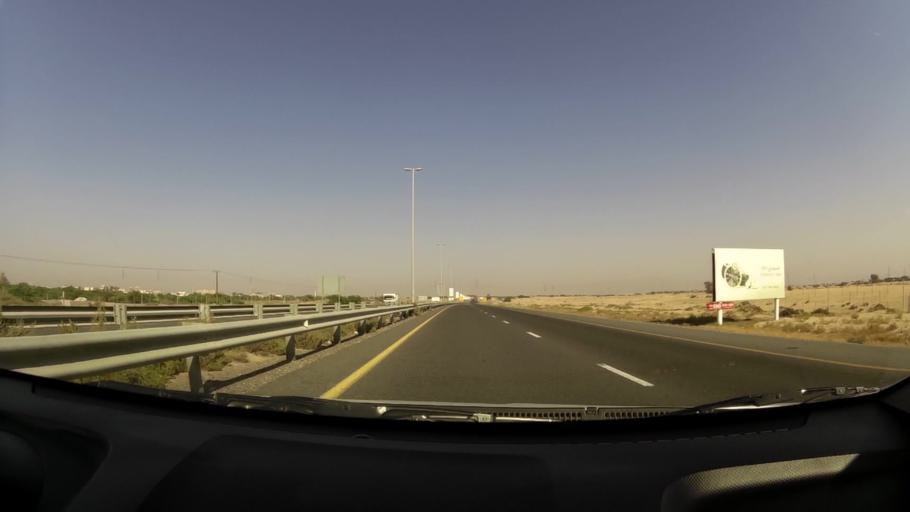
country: AE
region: Umm al Qaywayn
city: Umm al Qaywayn
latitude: 25.4761
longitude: 55.5718
